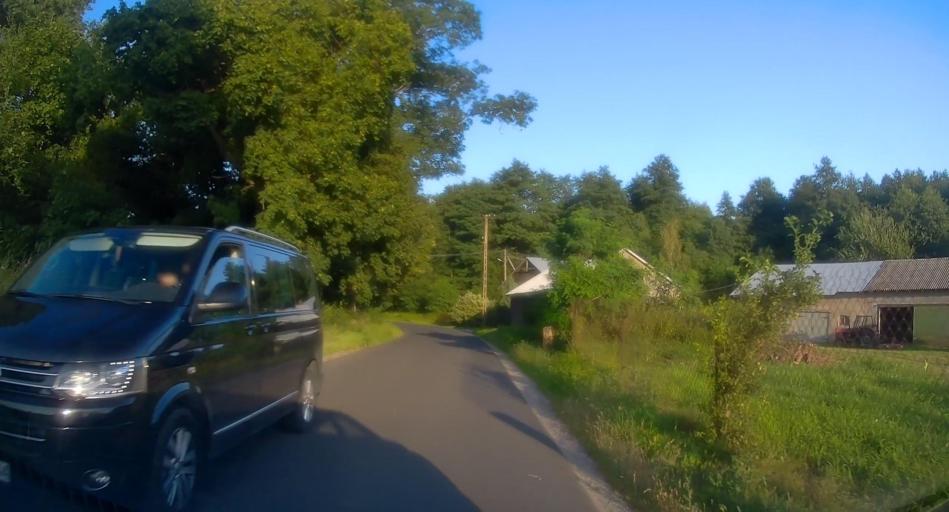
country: PL
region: Lodz Voivodeship
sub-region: Powiat skierniewicki
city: Kowiesy
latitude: 51.8885
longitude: 20.4129
